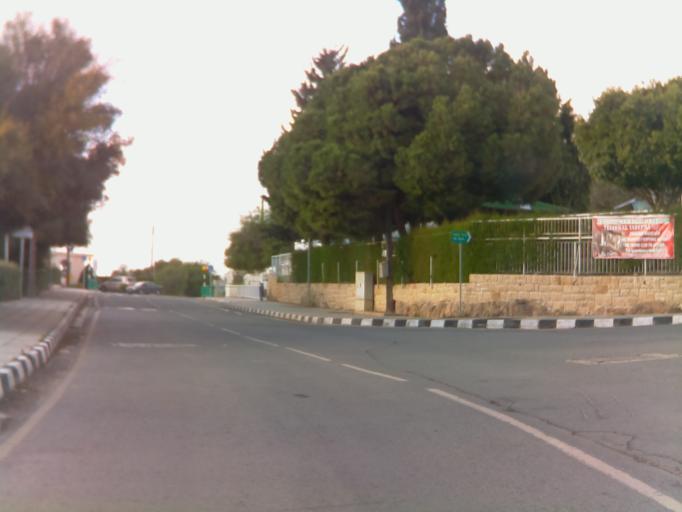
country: CY
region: Pafos
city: Kissonerga
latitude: 34.8241
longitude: 32.4016
